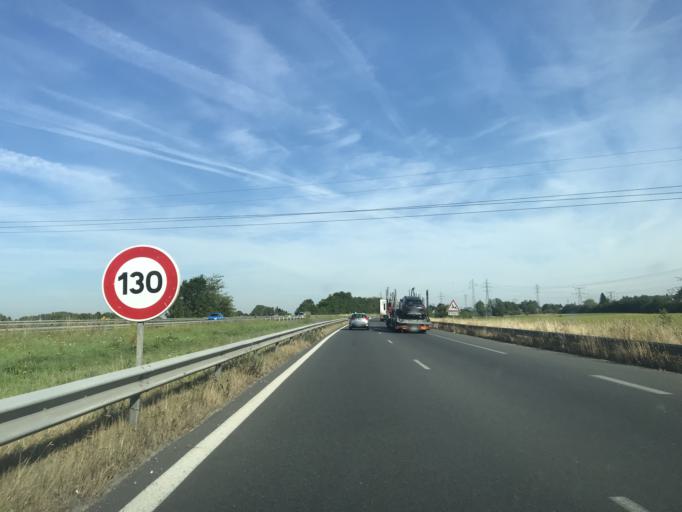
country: FR
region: Haute-Normandie
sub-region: Departement de la Seine-Maritime
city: La Vaupaliere
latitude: 49.4833
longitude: 1.0060
